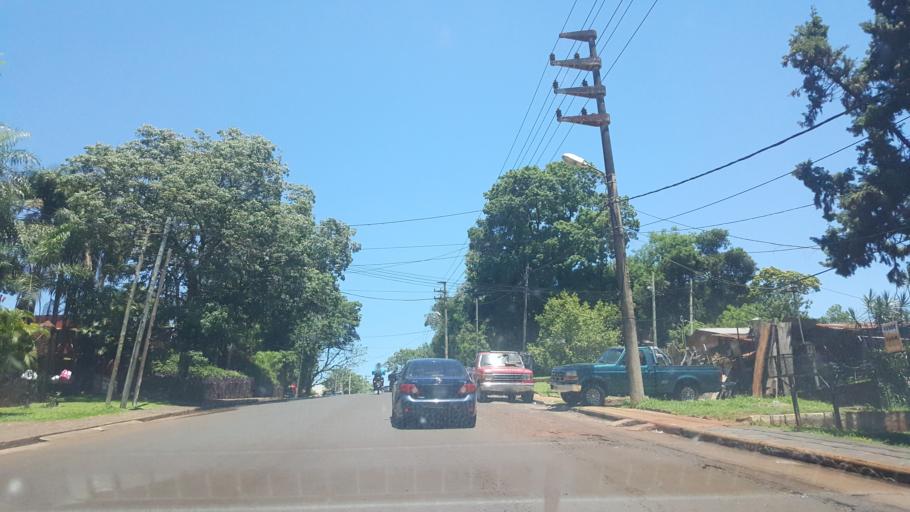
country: AR
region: Misiones
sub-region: Departamento de Capital
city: Posadas
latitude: -27.3601
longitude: -55.9080
